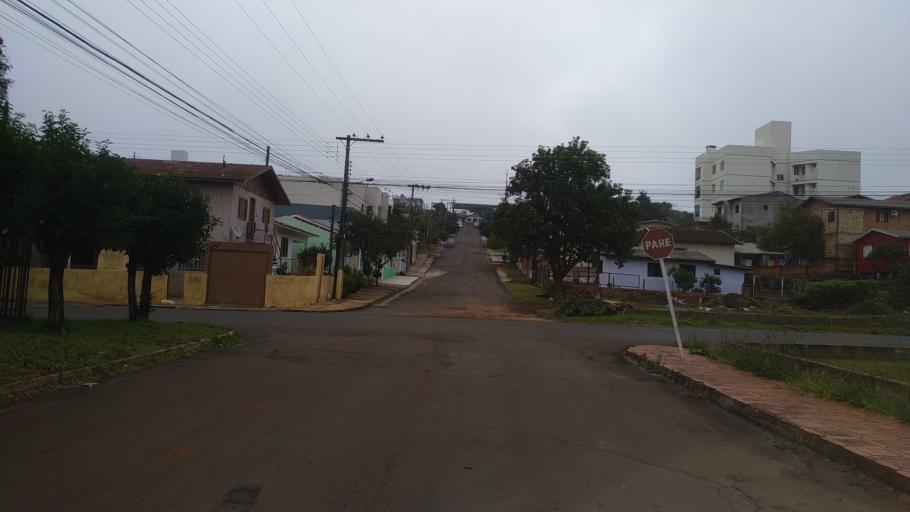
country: BR
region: Santa Catarina
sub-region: Chapeco
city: Chapeco
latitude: -27.0807
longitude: -52.6288
